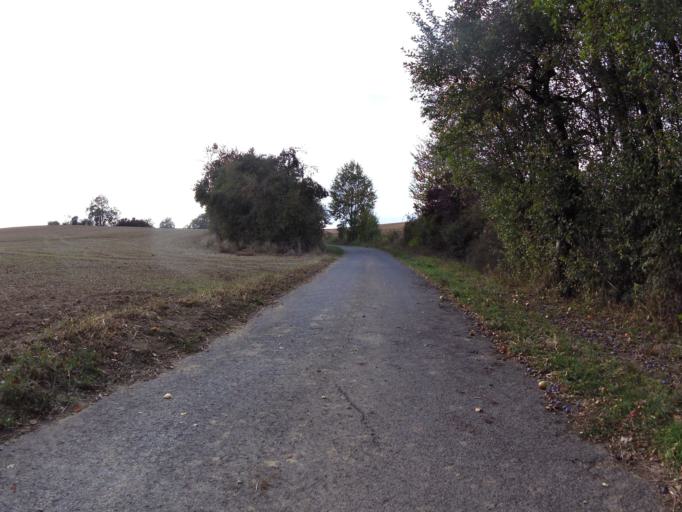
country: DE
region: Bavaria
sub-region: Regierungsbezirk Unterfranken
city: Reichenberg
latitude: 49.7255
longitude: 9.9518
